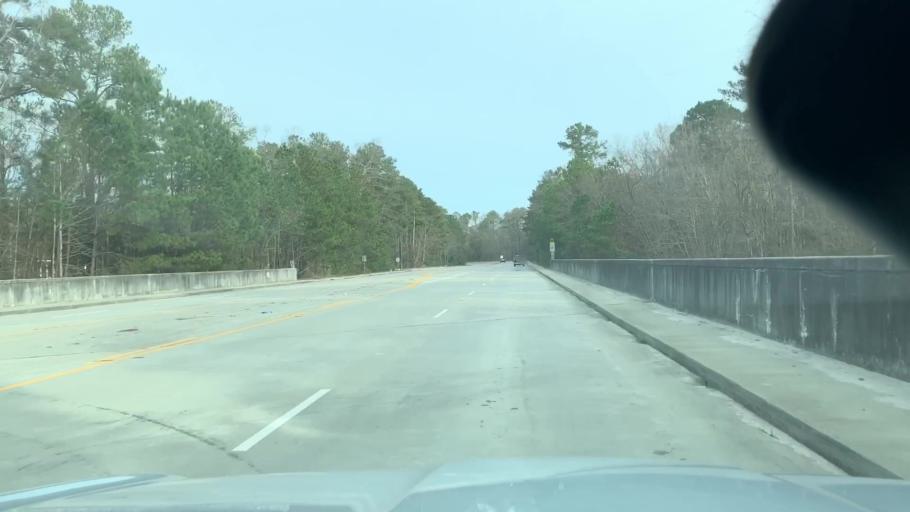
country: US
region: South Carolina
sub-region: Richland County
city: Dentsville
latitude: 34.0638
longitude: -80.9478
